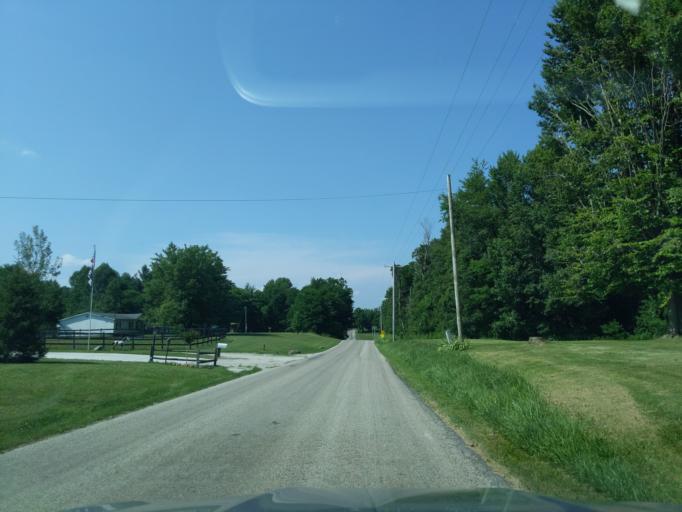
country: US
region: Indiana
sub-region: Ripley County
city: Osgood
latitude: 39.1489
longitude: -85.3383
